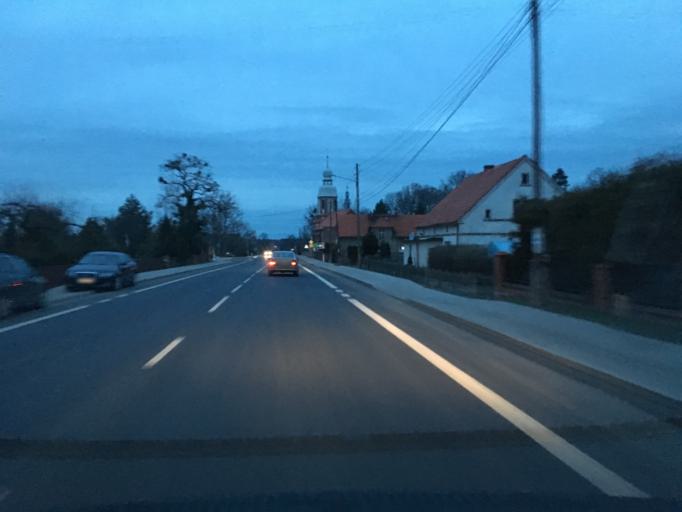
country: PL
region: Opole Voivodeship
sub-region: Powiat opolski
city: Dabrowa
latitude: 50.7214
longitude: 17.7635
